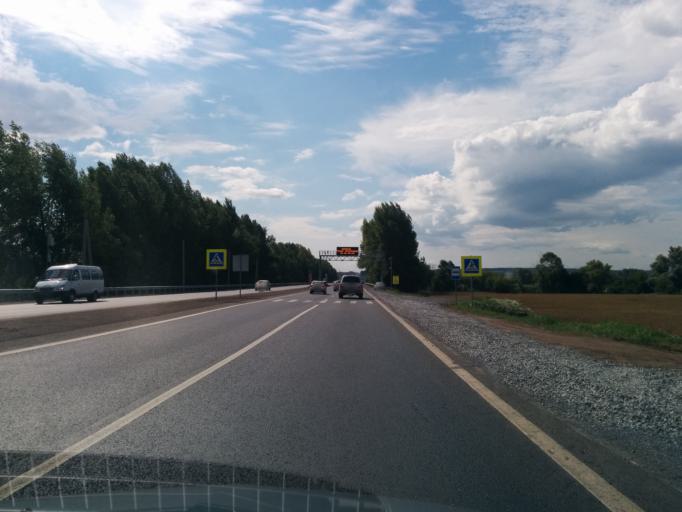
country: RU
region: Bashkortostan
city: Avdon
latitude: 54.5136
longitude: 55.8989
